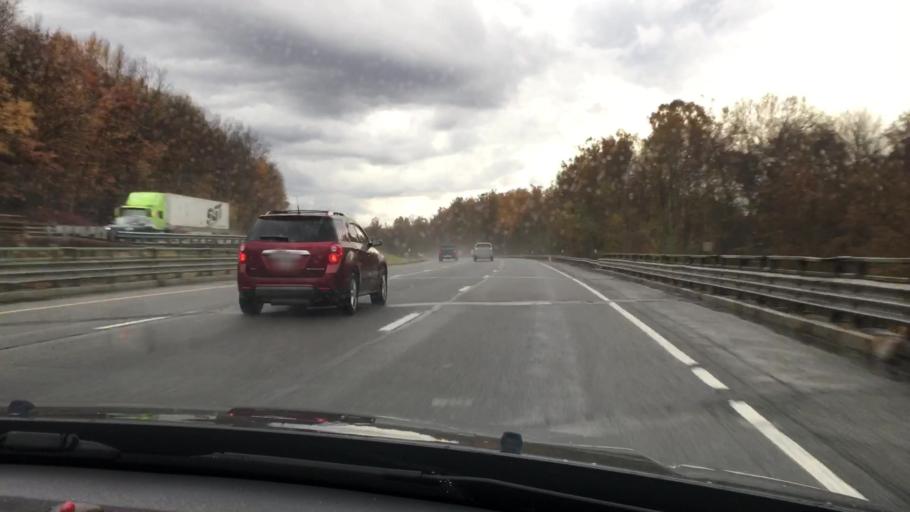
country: US
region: New York
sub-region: Rockland County
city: Sloatsburg
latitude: 41.2280
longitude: -74.1816
